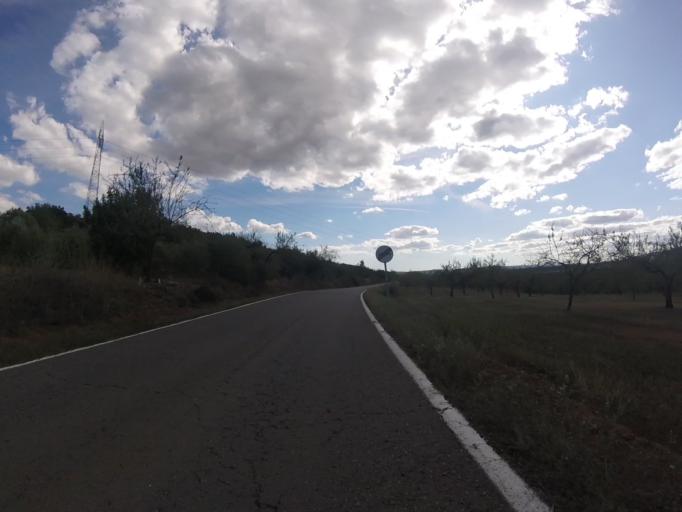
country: ES
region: Valencia
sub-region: Provincia de Castello
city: Cuevas de Vinroma
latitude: 40.3601
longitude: 0.1250
